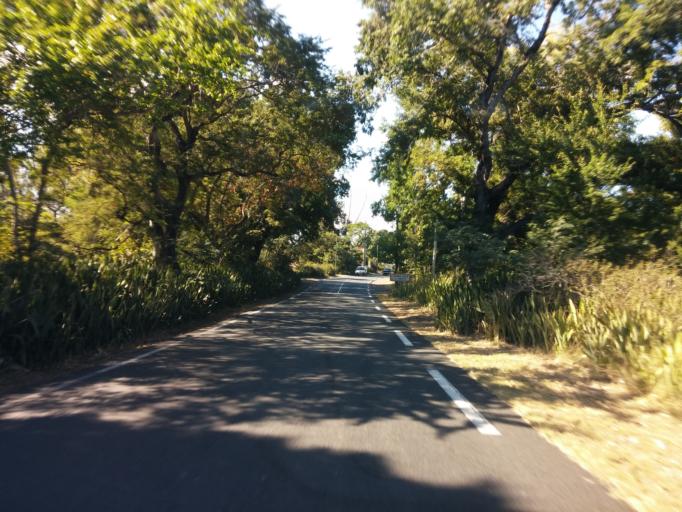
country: RE
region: Reunion
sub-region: Reunion
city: Les Avirons
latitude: -21.2614
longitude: 55.3531
